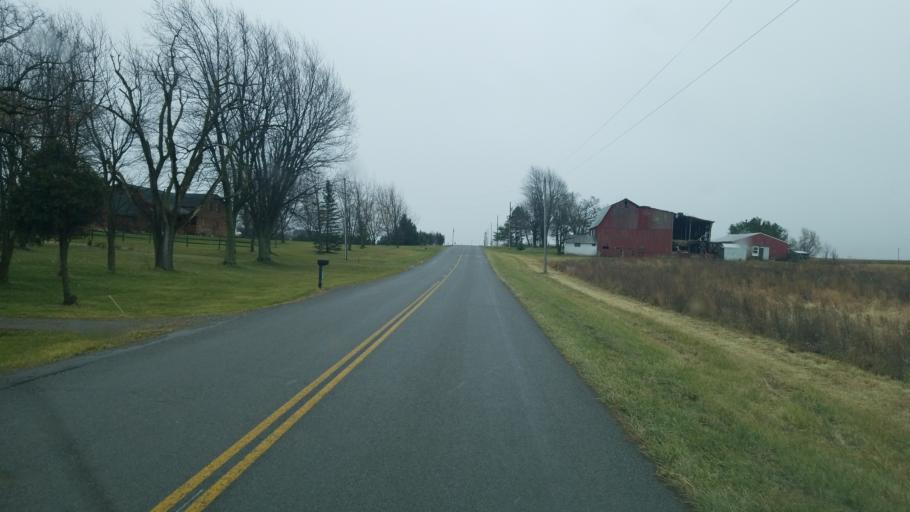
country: US
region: Ohio
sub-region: Logan County
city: Northwood
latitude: 40.4484
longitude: -83.6544
